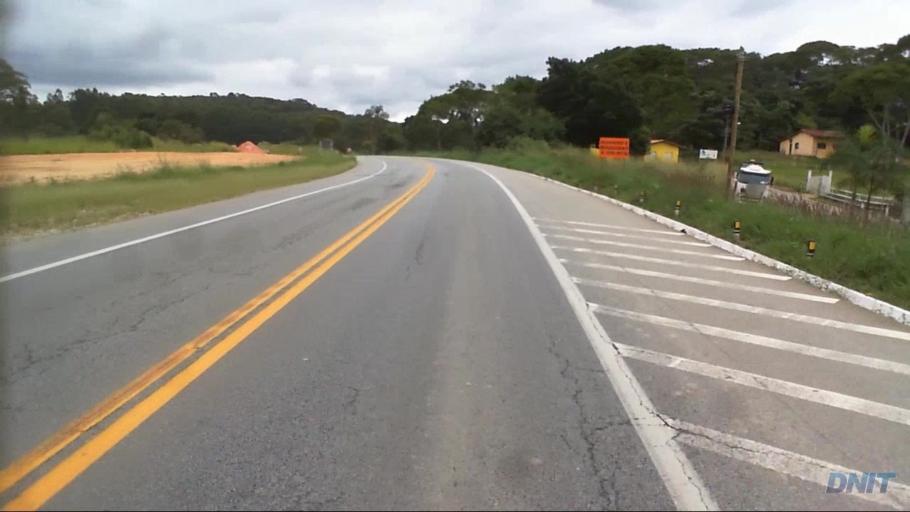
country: BR
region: Minas Gerais
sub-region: Barao De Cocais
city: Barao de Cocais
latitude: -19.7678
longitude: -43.4532
